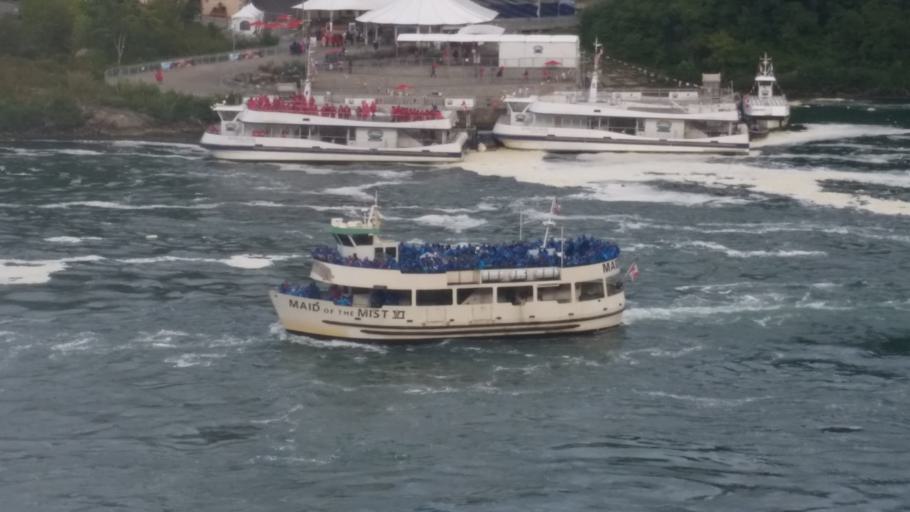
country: US
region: New York
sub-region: Niagara County
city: Niagara Falls
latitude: 43.0856
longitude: -79.0681
